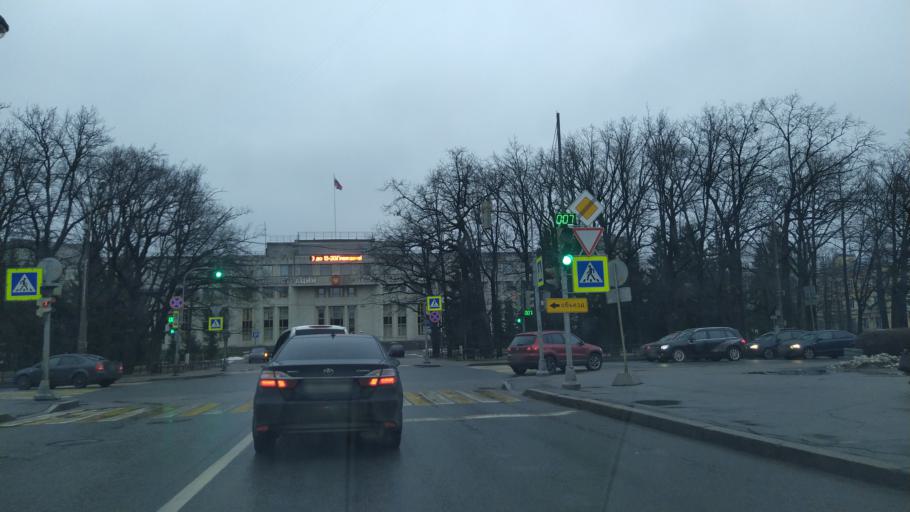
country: RU
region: St.-Petersburg
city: Pushkin
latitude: 59.7217
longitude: 30.4159
